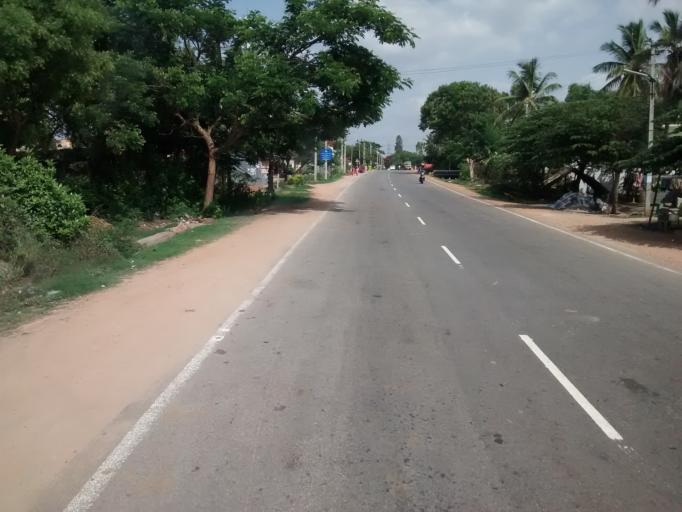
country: IN
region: Karnataka
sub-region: Mysore
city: Hunsur
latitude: 12.3654
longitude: 76.4186
